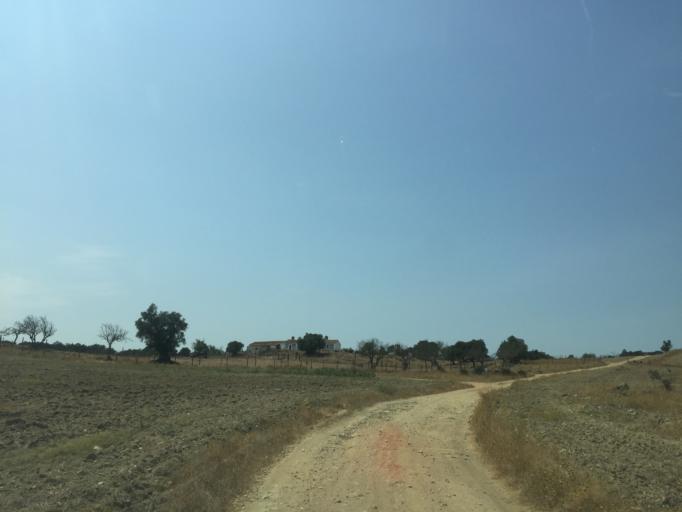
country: PT
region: Setubal
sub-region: Grandola
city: Grandola
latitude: 38.0439
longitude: -8.4762
